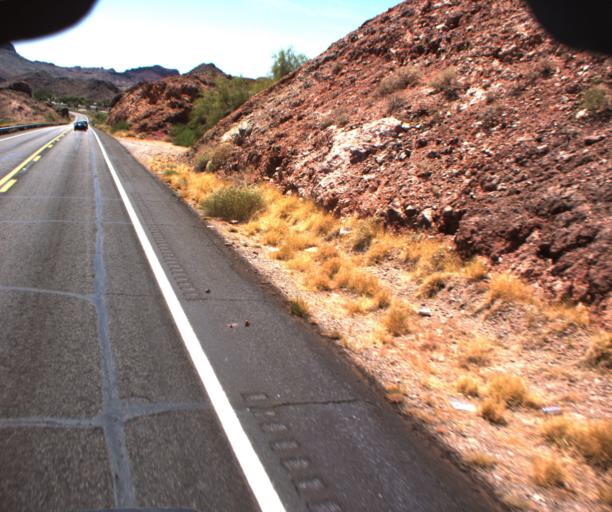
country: US
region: Arizona
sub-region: La Paz County
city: Cienega Springs
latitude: 34.2744
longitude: -114.1313
